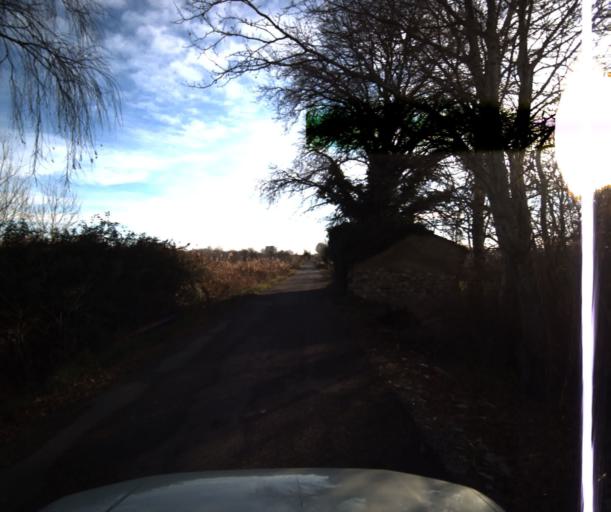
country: FR
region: Provence-Alpes-Cote d'Azur
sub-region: Departement du Vaucluse
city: Pertuis
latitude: 43.6737
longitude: 5.4897
